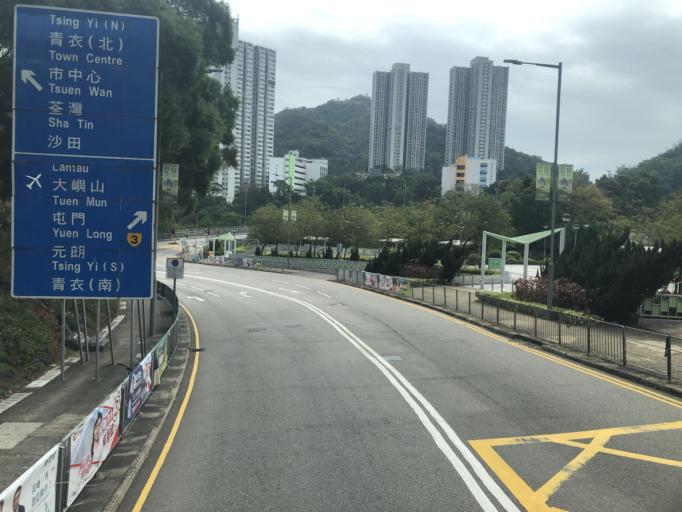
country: HK
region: Tsuen Wan
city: Tsuen Wan
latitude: 22.3531
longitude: 114.0977
